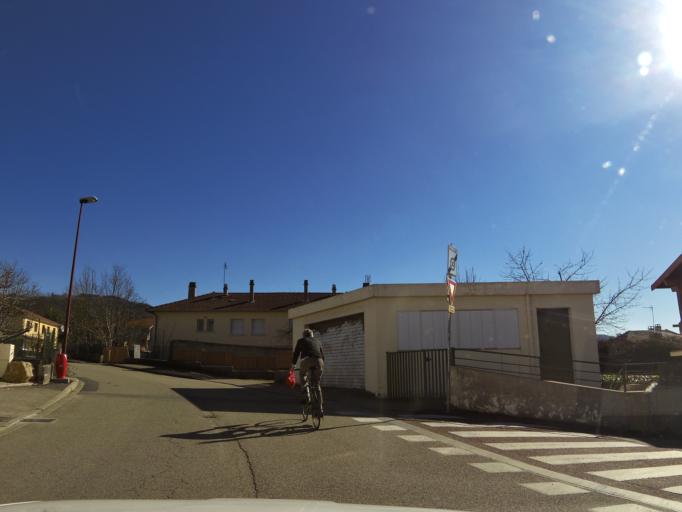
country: FR
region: Rhone-Alpes
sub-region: Departement de l'Ain
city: Amberieu-en-Bugey
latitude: 45.9595
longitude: 5.3605
